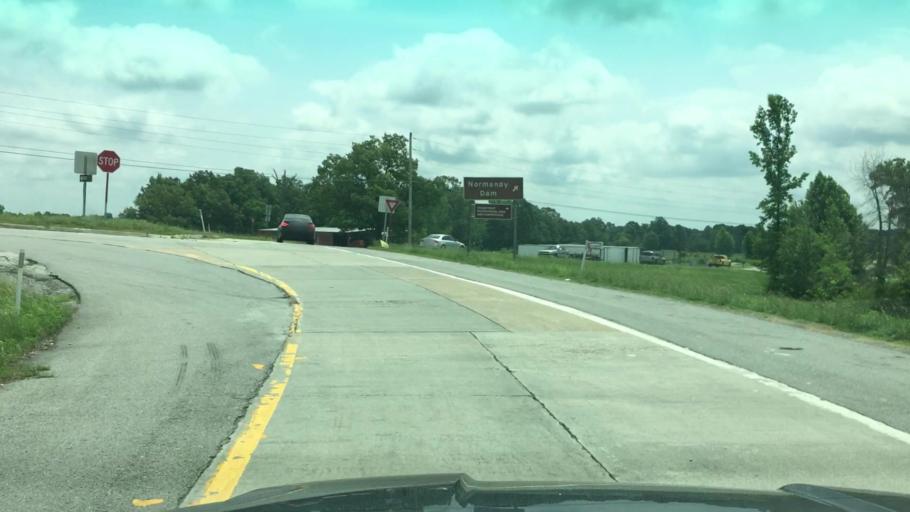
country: US
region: Tennessee
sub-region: Coffee County
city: New Union
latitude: 35.5337
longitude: -86.1629
